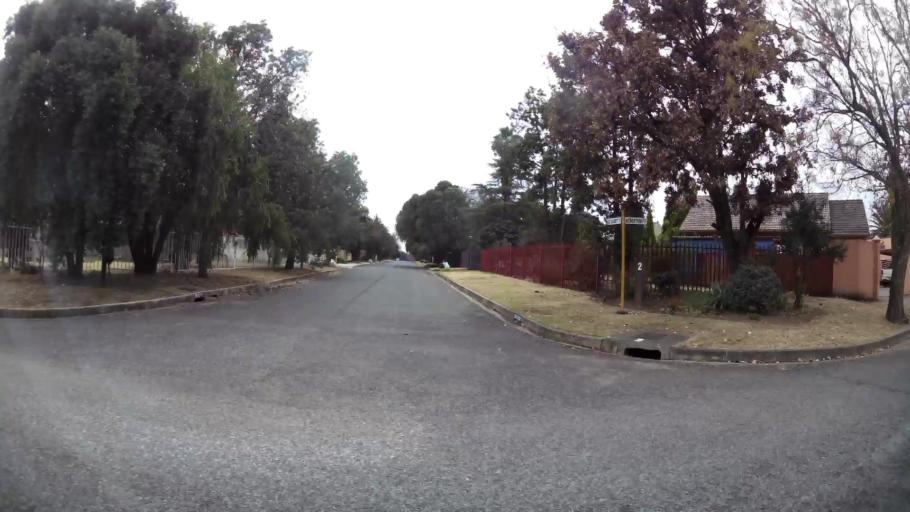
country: ZA
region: Orange Free State
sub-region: Fezile Dabi District Municipality
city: Kroonstad
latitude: -27.6753
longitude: 27.2485
